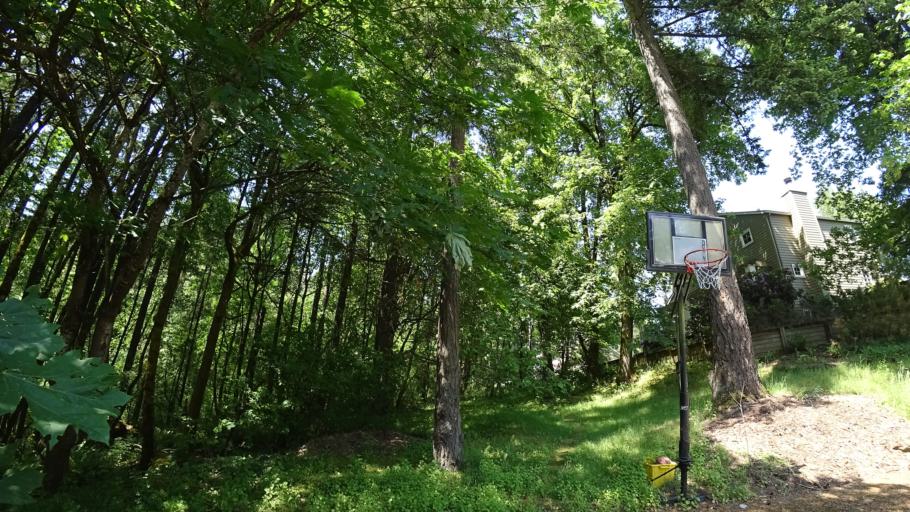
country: US
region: Oregon
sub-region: Washington County
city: Metzger
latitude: 45.4446
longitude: -122.7166
